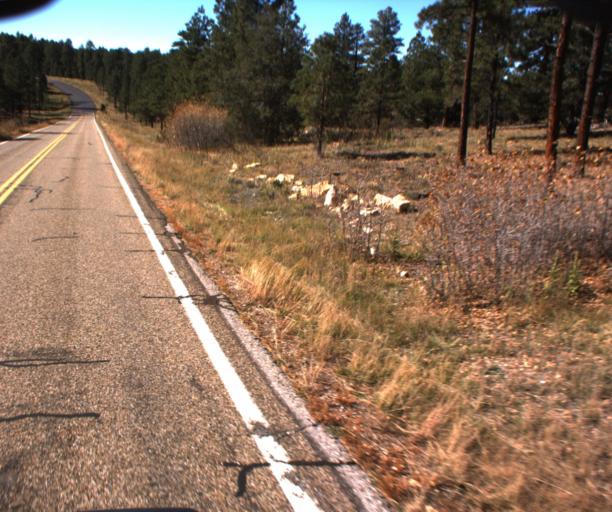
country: US
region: Arizona
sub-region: Coconino County
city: Fredonia
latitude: 36.7583
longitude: -112.2666
